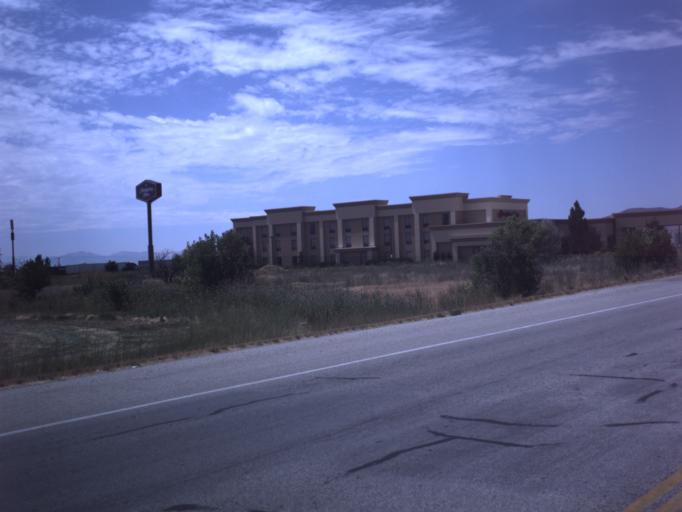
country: US
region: Utah
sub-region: Box Elder County
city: Tremonton
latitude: 41.7110
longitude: -112.1966
